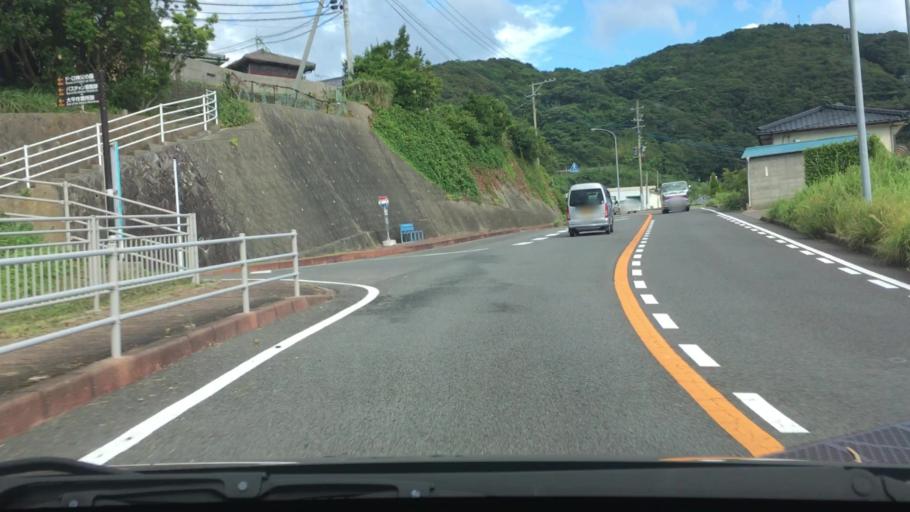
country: JP
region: Nagasaki
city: Togitsu
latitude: 32.8426
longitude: 129.7028
